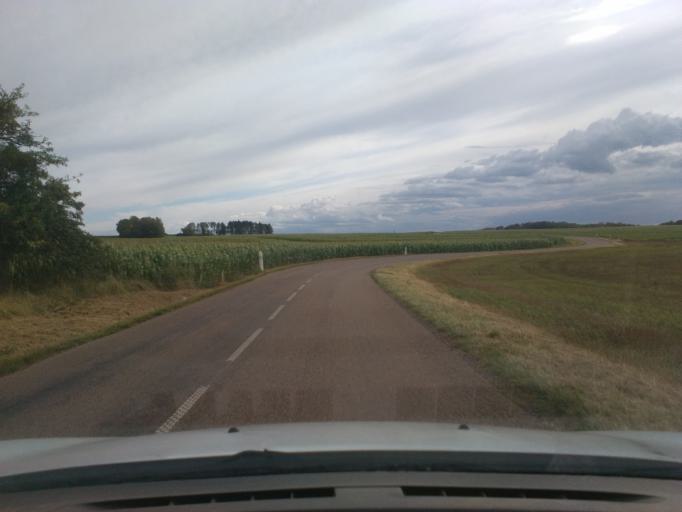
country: FR
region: Lorraine
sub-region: Departement des Vosges
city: Chatel-sur-Moselle
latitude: 48.3391
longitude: 6.4236
